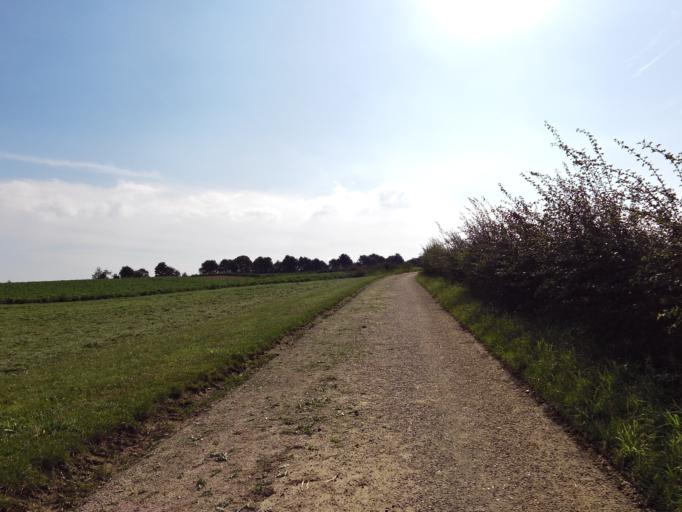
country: NL
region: Limburg
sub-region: Gemeente Voerendaal
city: Klimmen
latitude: 50.8598
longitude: 5.9005
